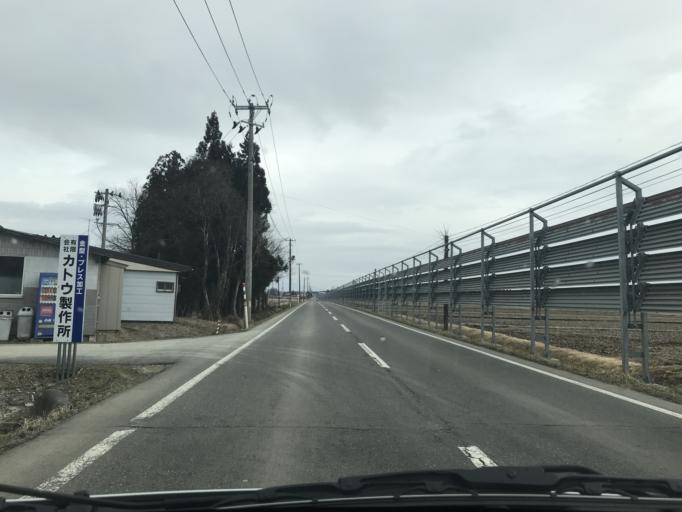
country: JP
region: Iwate
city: Kitakami
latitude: 39.3128
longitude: 141.0213
